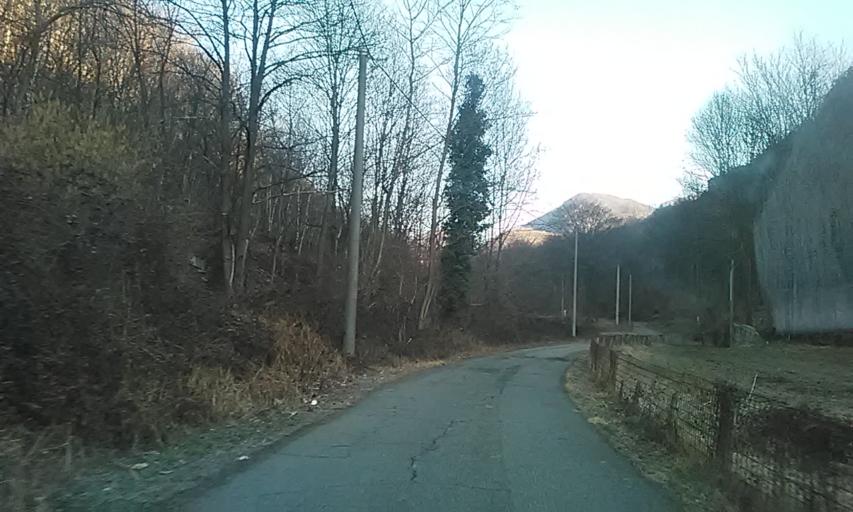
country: IT
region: Piedmont
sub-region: Provincia di Vercelli
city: Quarona
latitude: 45.7679
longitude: 8.2724
